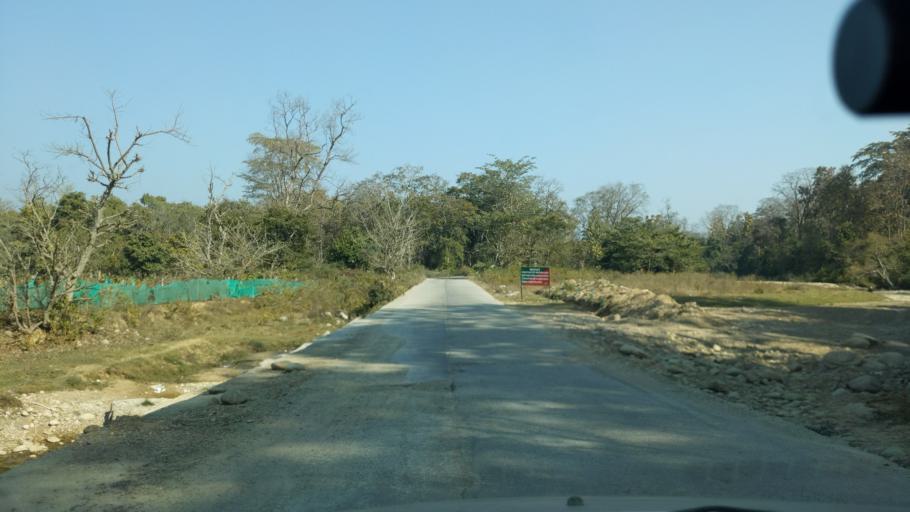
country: IN
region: Uttarakhand
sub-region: Naini Tal
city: Ramnagar
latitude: 29.4099
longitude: 79.1368
